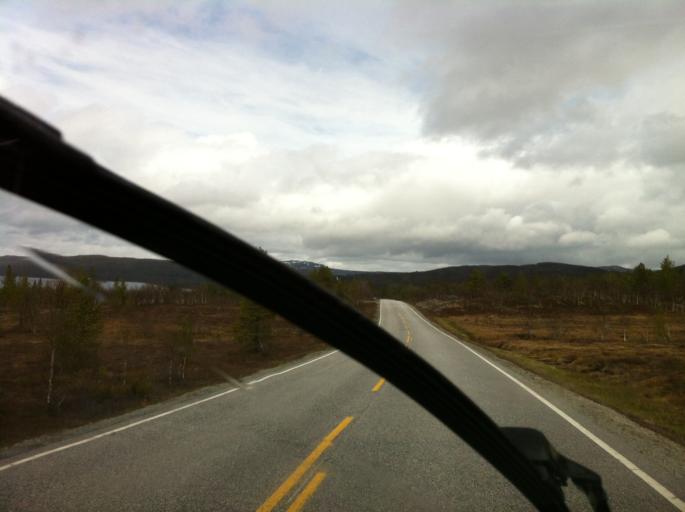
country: NO
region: Sor-Trondelag
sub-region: Roros
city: Roros
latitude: 62.5970
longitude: 11.7427
